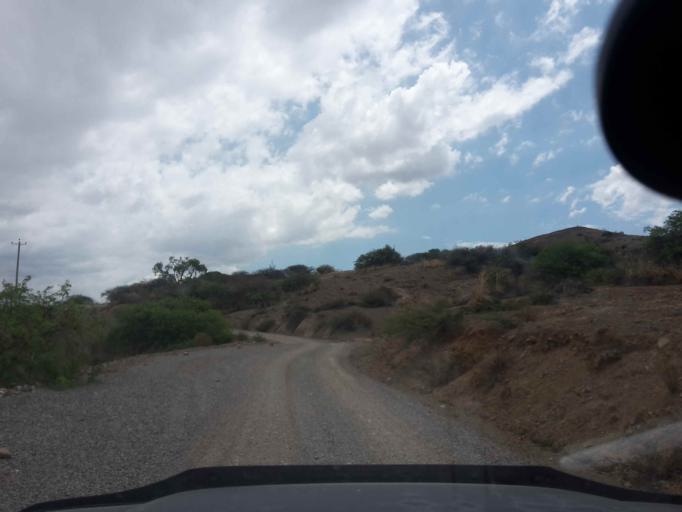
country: BO
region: Cochabamba
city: Sipe Sipe
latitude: -17.5437
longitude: -66.4803
